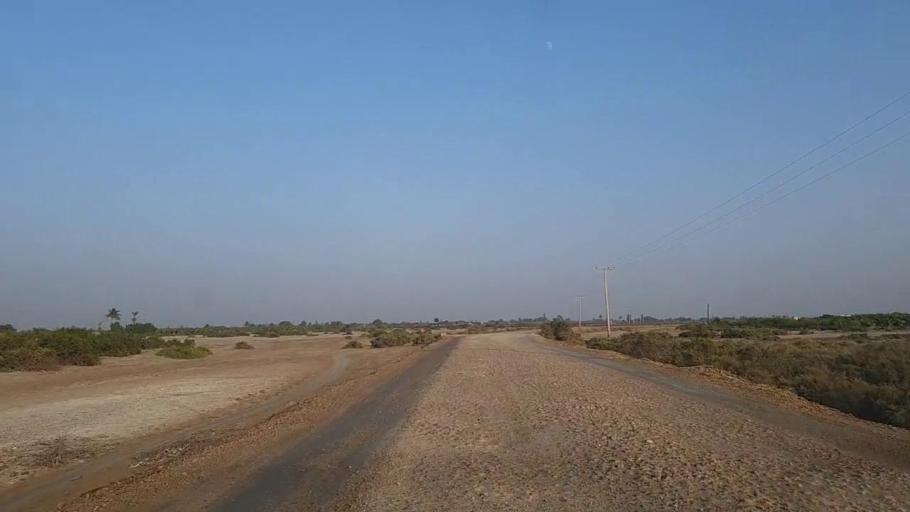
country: PK
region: Sindh
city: Keti Bandar
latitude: 24.2792
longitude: 67.6406
